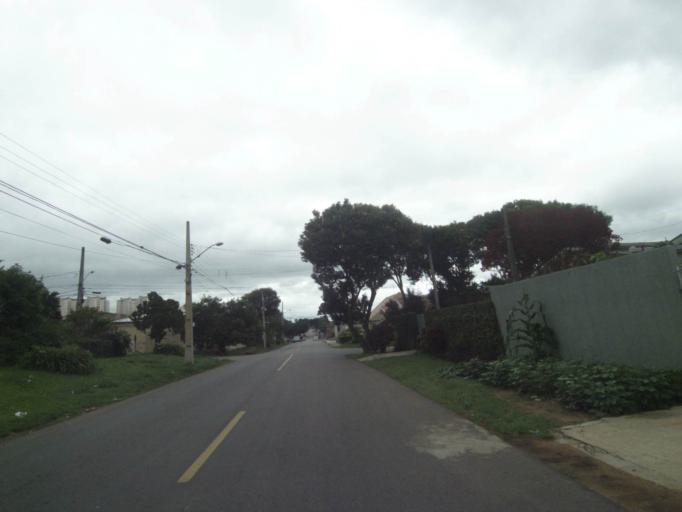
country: BR
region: Parana
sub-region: Curitiba
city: Curitiba
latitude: -25.4931
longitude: -49.2996
